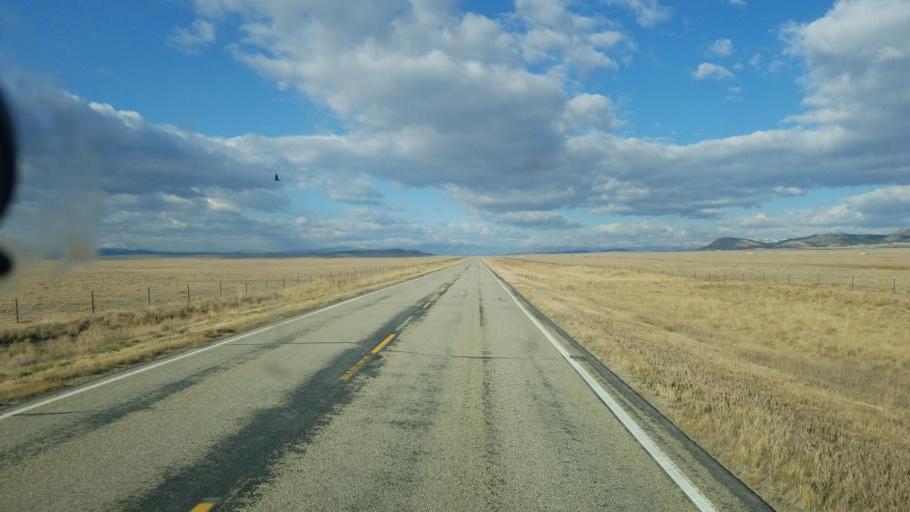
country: US
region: Colorado
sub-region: Park County
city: Fairplay
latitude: 39.0463
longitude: -105.6602
